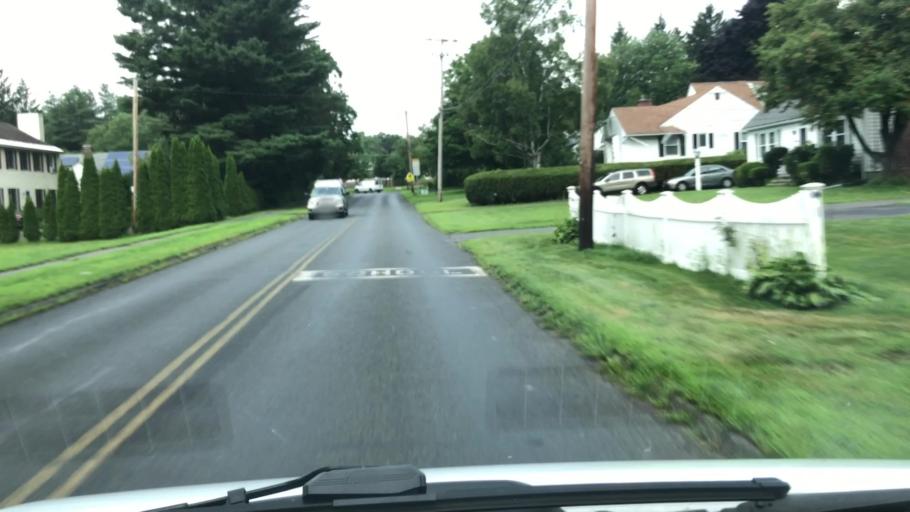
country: US
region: Massachusetts
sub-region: Hampshire County
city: Northampton
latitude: 42.3340
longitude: -72.6424
